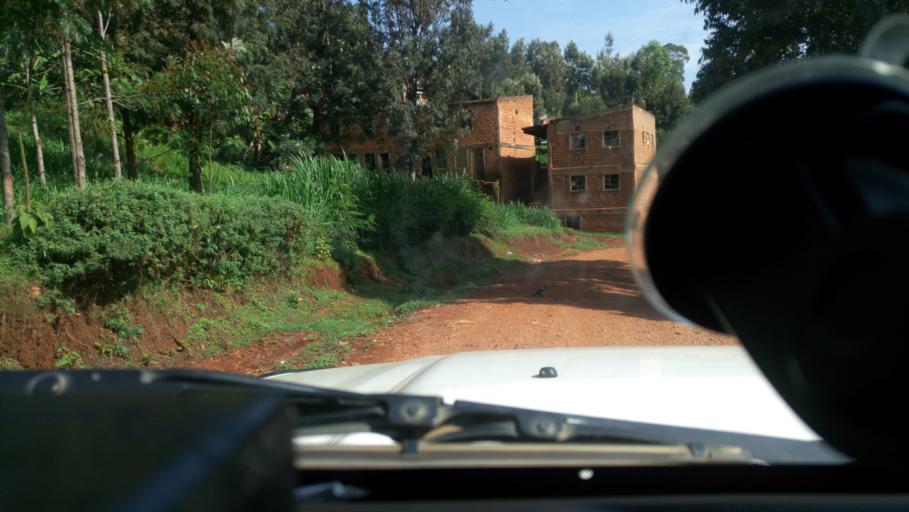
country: KE
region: Nyamira District
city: Nyamira
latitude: -0.5571
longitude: 34.9322
